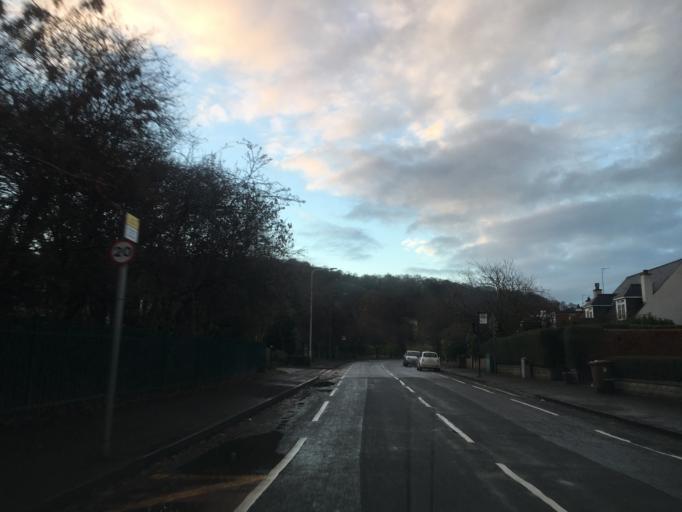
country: GB
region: Scotland
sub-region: Edinburgh
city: Colinton
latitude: 55.9558
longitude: -3.2624
